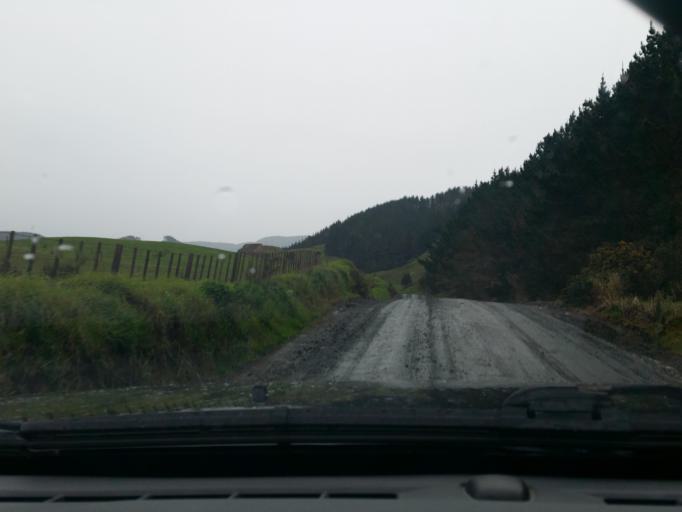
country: NZ
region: Northland
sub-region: Kaipara District
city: Dargaville
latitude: -35.8221
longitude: 173.8158
